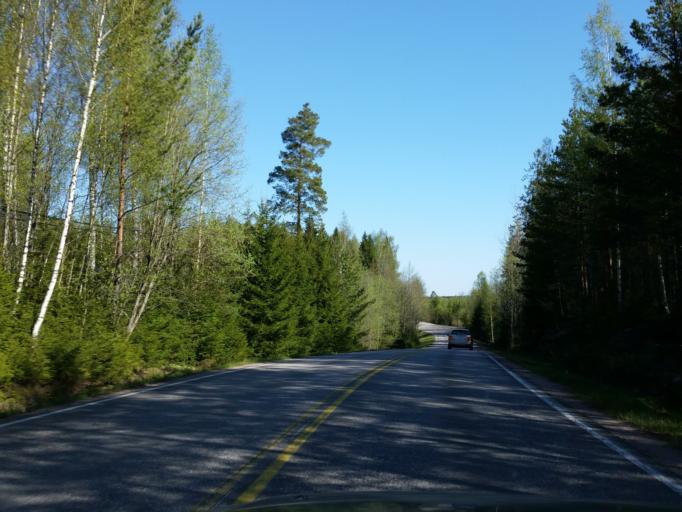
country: FI
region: Uusimaa
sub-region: Helsinki
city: Kirkkonummi
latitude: 60.1924
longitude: 24.3939
